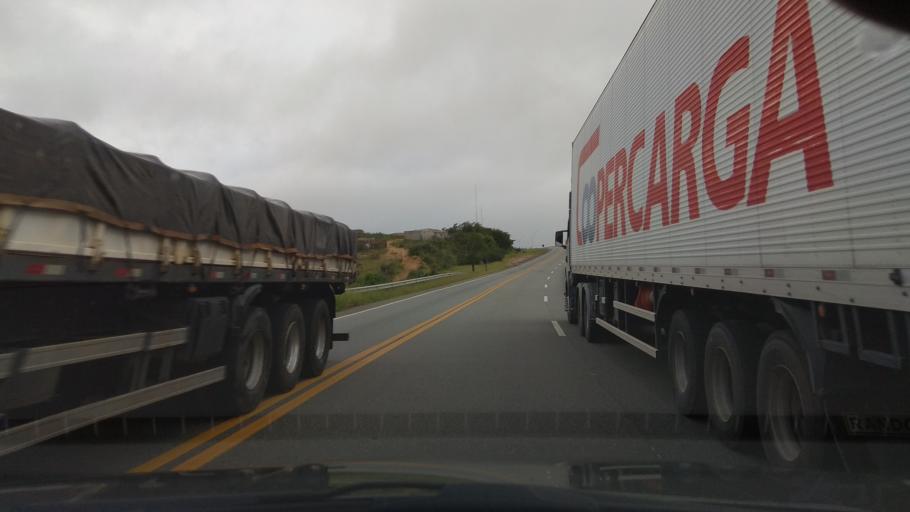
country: BR
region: Bahia
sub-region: Santa Ines
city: Santa Ines
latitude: -13.0640
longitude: -39.9578
